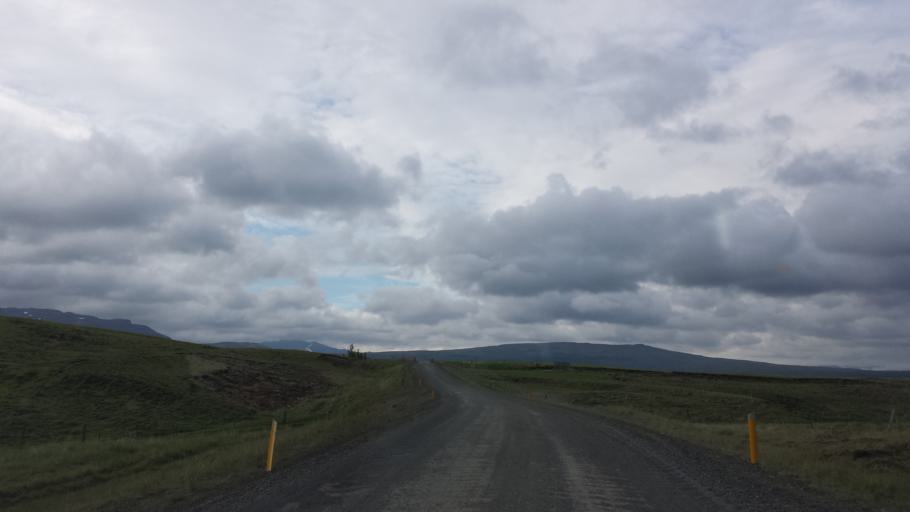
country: IS
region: South
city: Vestmannaeyjar
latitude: 64.2864
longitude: -20.2259
